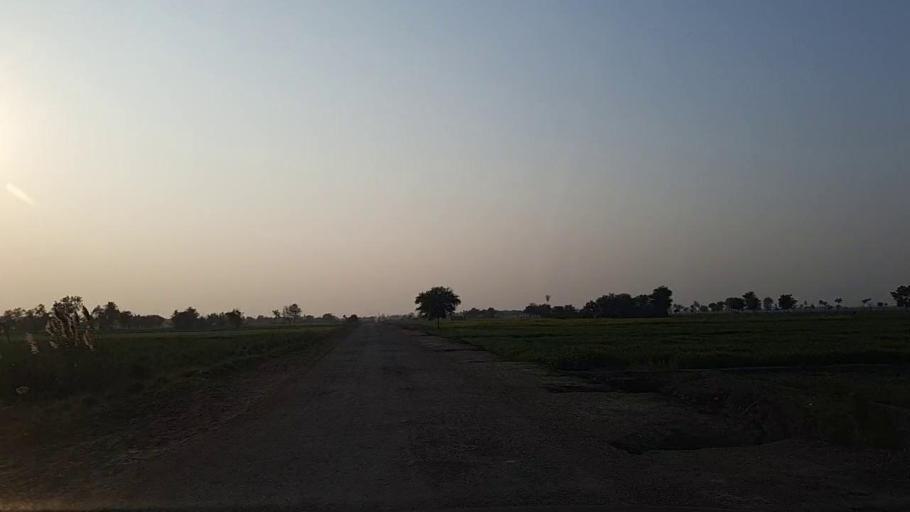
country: PK
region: Sindh
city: Daur
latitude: 26.4165
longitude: 68.3783
